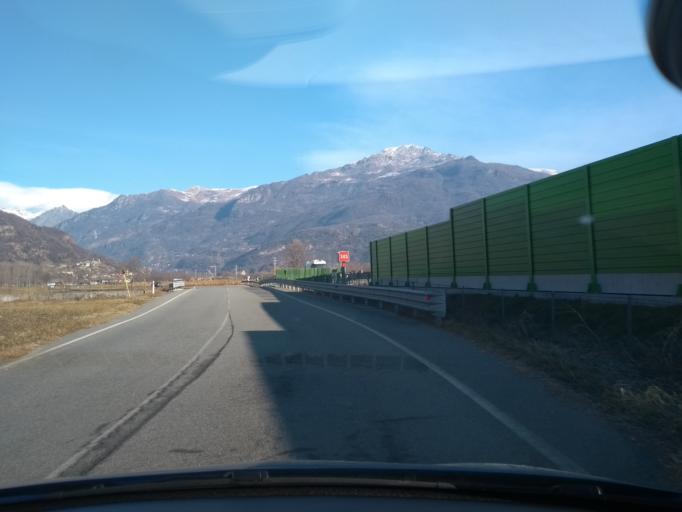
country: IT
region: Piedmont
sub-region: Provincia di Torino
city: Quassolo
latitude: 45.5103
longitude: 7.8327
